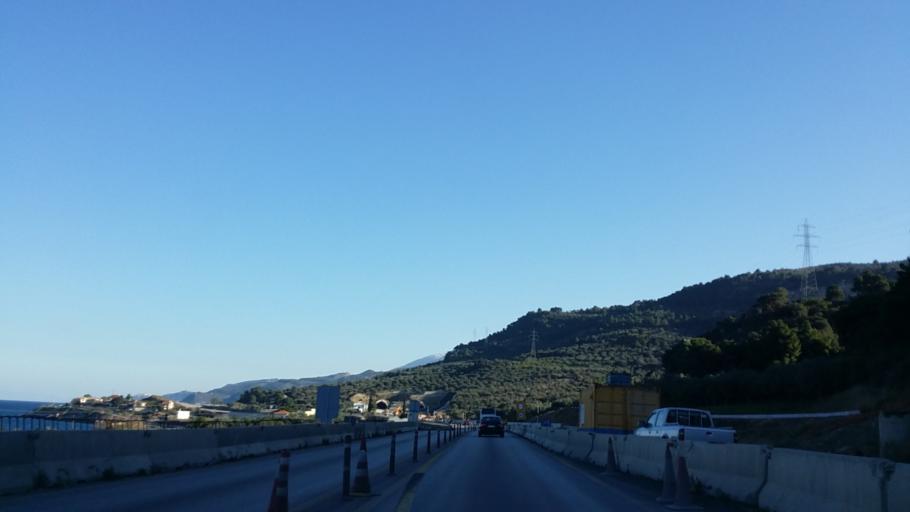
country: GR
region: West Greece
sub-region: Nomos Achaias
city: Aiyira
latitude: 38.1434
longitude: 22.3676
